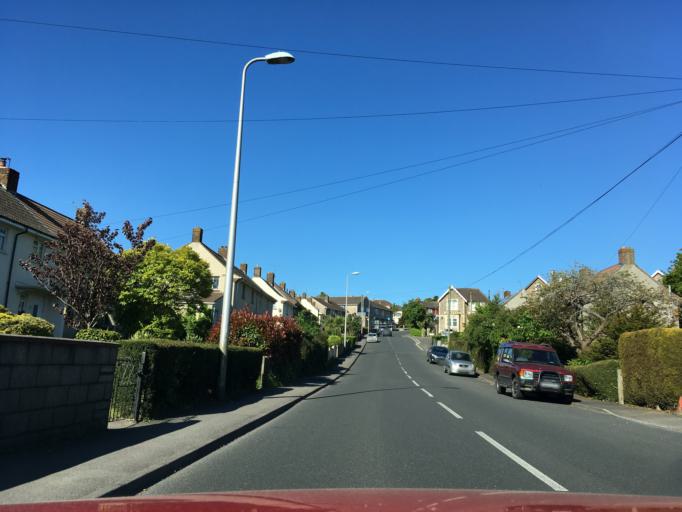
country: GB
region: England
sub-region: North Somerset
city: Portishead
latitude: 51.4818
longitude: -2.7791
